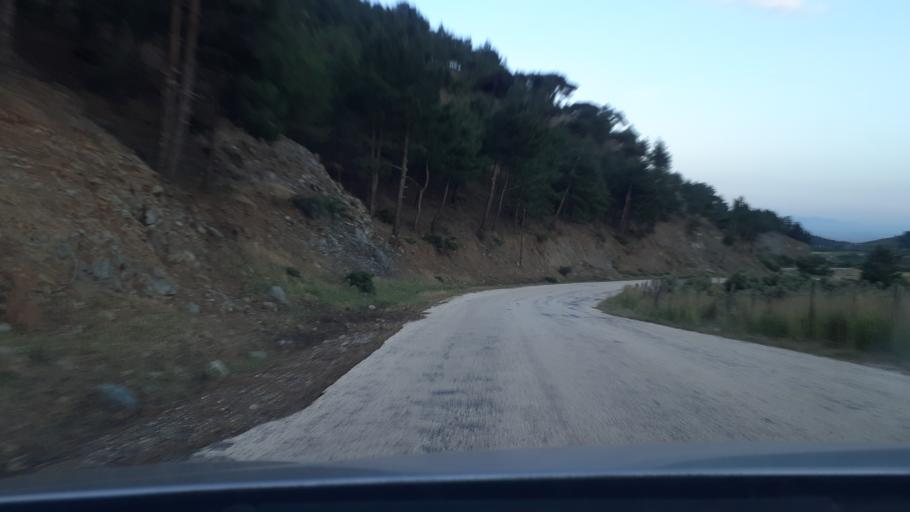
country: TR
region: Hatay
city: Kirikhan
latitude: 36.5159
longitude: 36.3188
